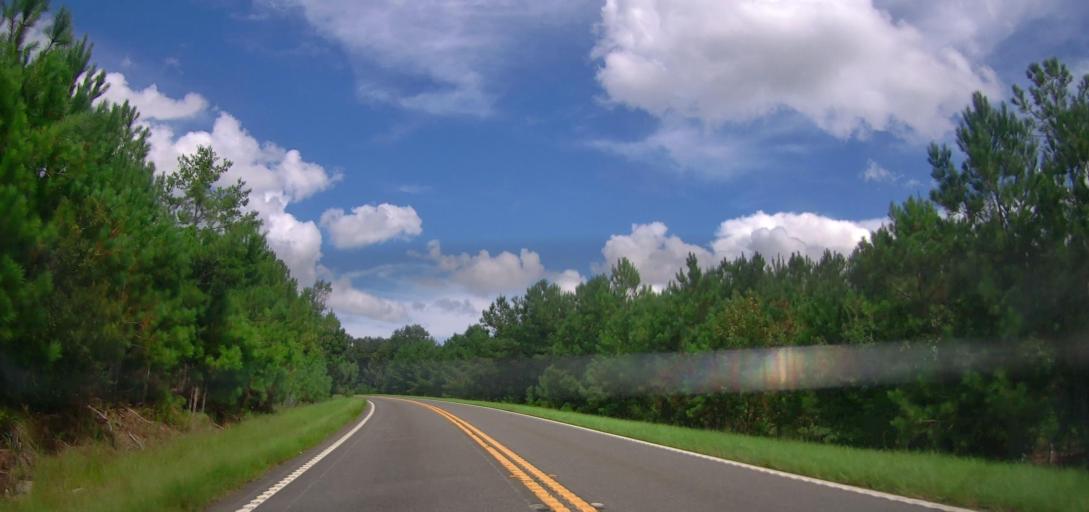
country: US
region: Georgia
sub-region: Taylor County
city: Reynolds
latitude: 32.4378
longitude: -84.1497
